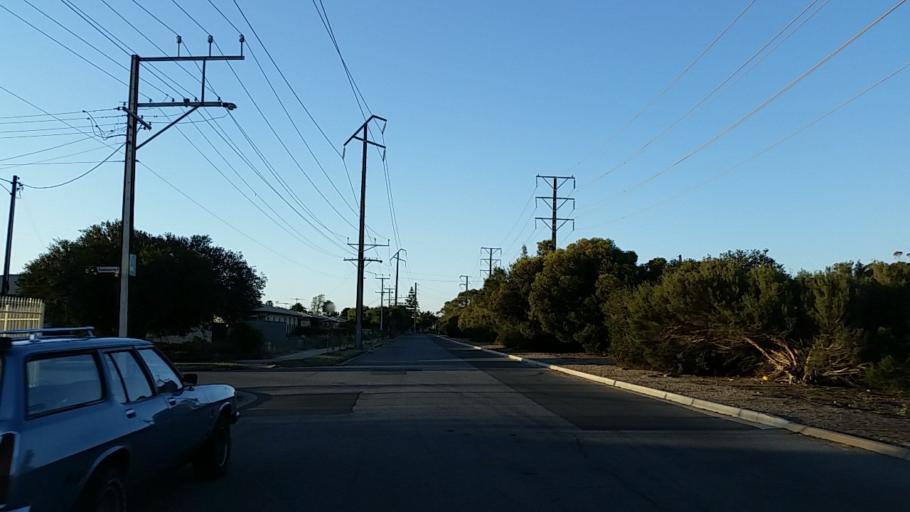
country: AU
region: South Australia
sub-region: Port Adelaide Enfield
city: Birkenhead
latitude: -34.8052
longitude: 138.5061
